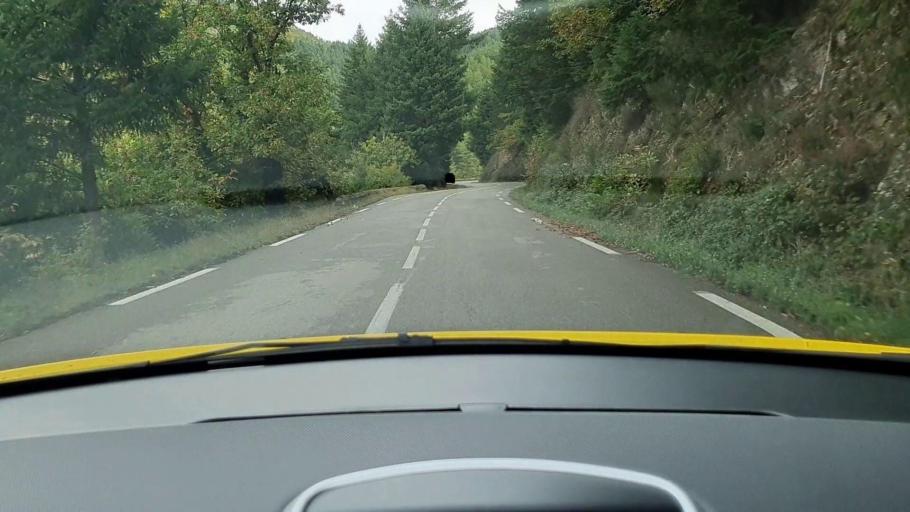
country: FR
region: Languedoc-Roussillon
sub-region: Departement du Gard
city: Le Vigan
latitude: 44.0178
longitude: 3.5989
